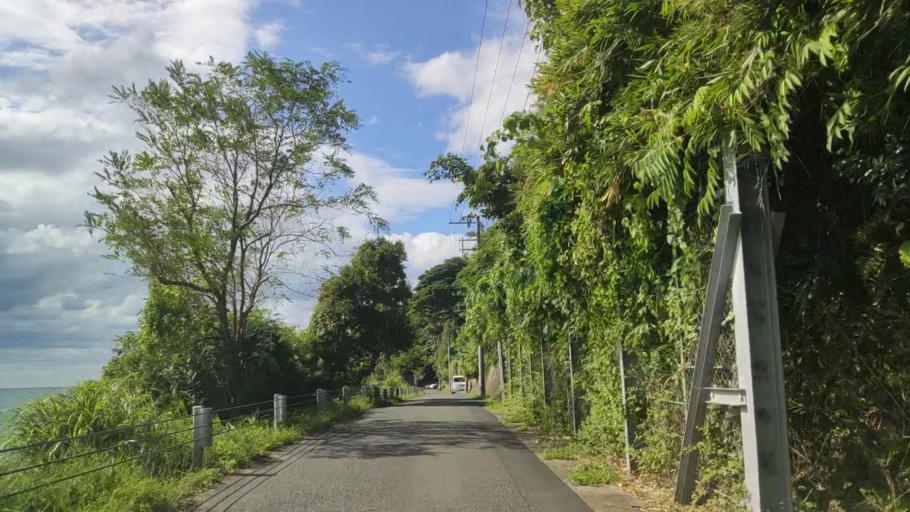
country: JP
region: Hyogo
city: Toyooka
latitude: 35.6700
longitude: 134.9667
